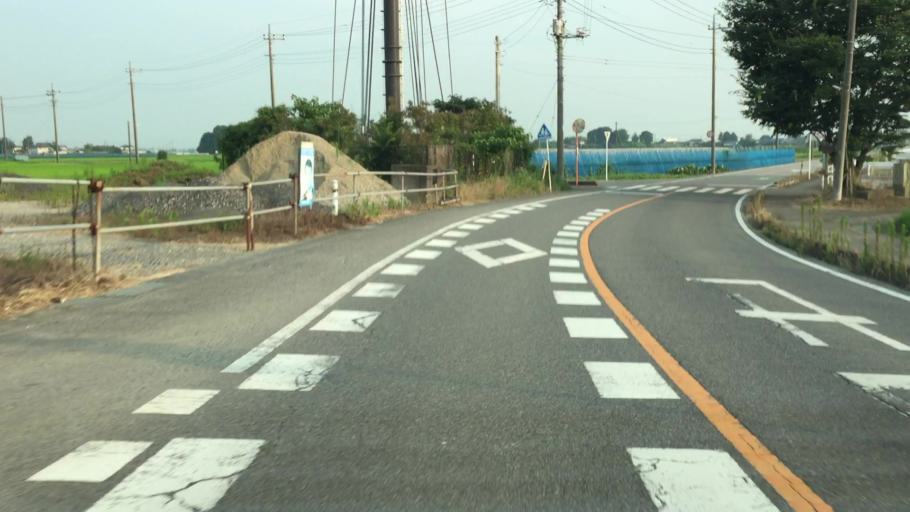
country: JP
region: Tochigi
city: Fujioka
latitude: 36.2576
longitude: 139.6213
